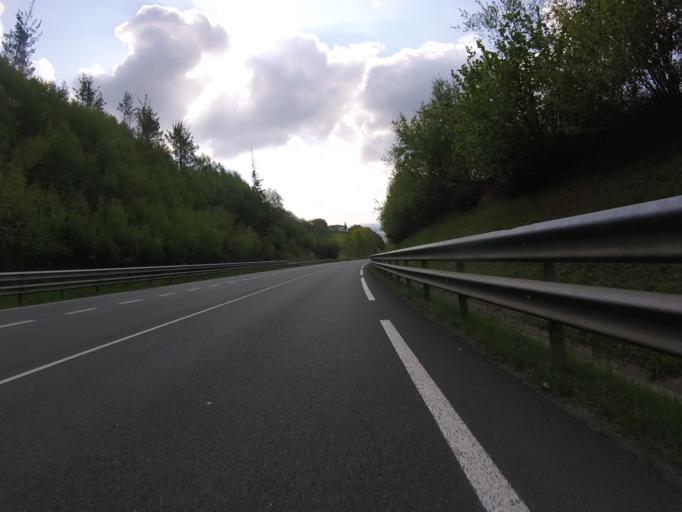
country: ES
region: Basque Country
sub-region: Provincia de Guipuzcoa
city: Azkoitia
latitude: 43.1974
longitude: -2.3391
